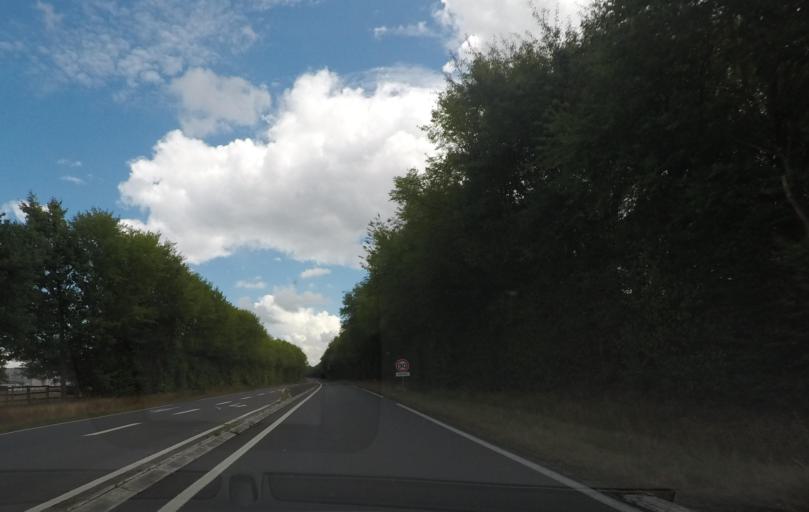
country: FR
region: Pays de la Loire
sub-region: Departement de la Sarthe
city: Champagne
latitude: 48.0725
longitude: 0.3016
